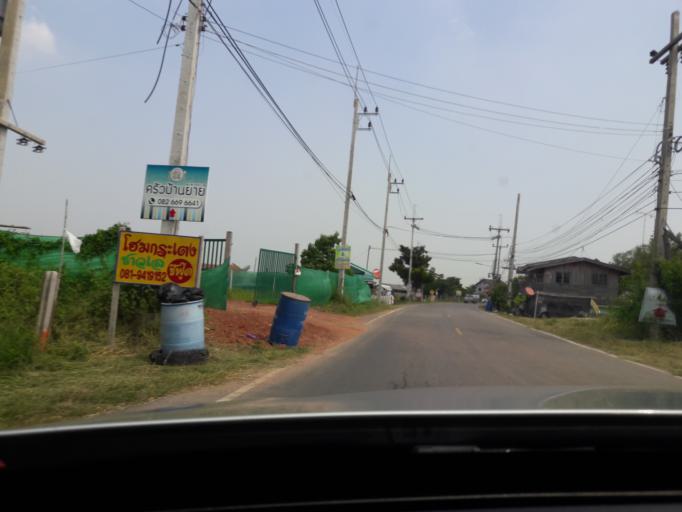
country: TH
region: Samut Songkhram
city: Amphawa
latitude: 13.3389
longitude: 99.9576
